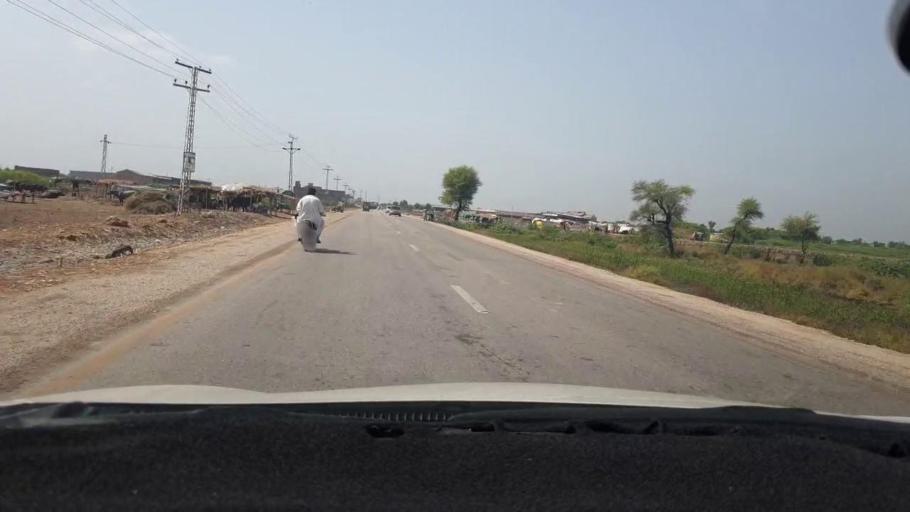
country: PK
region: Sindh
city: Mirpur Khas
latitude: 25.5531
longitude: 69.0502
